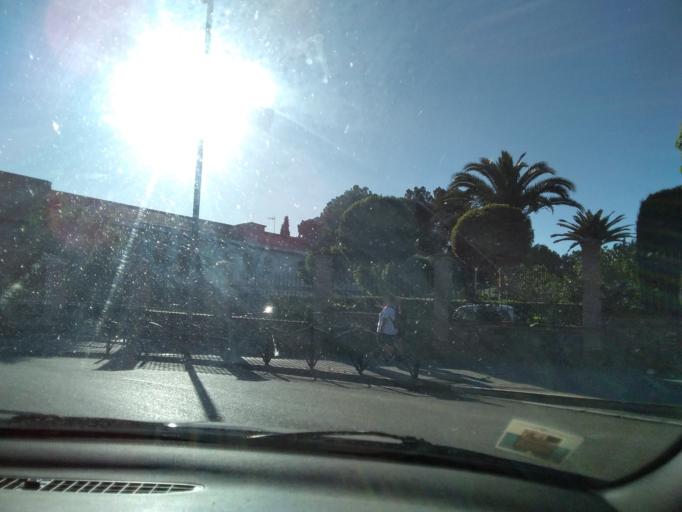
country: ES
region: Castille-La Mancha
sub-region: Province of Toledo
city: Toledo
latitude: 39.8745
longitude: -4.0370
